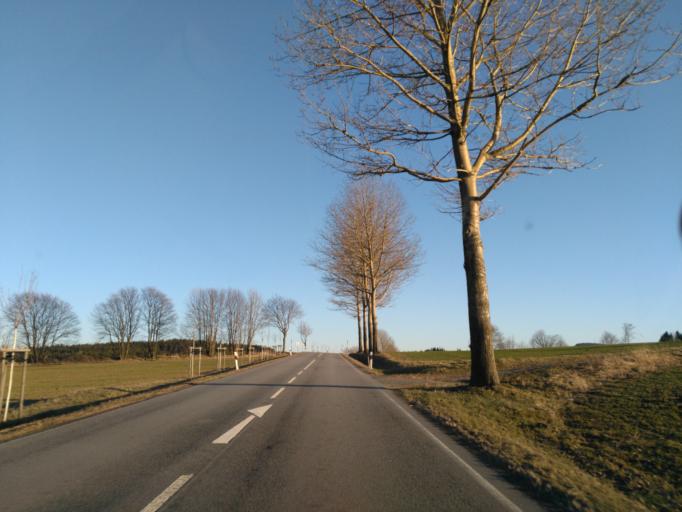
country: DE
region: Saxony
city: Konigswalde
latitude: 50.5421
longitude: 13.0215
